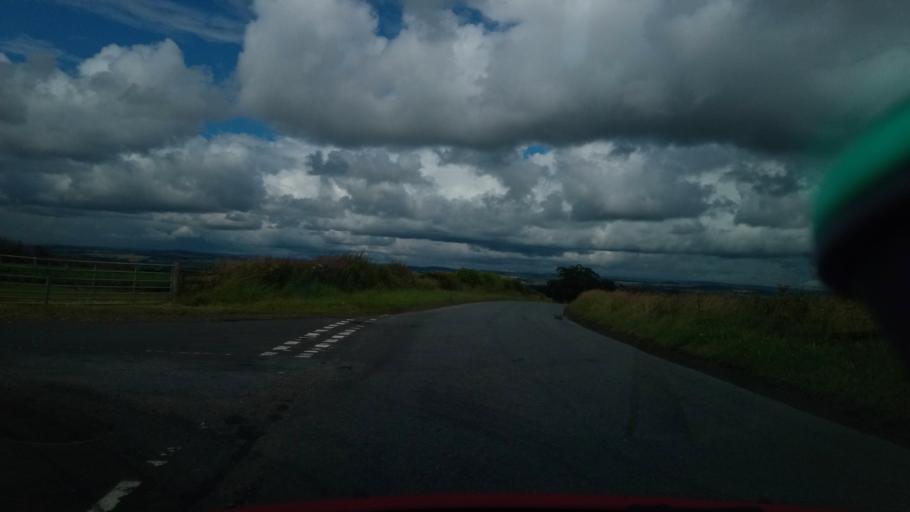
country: GB
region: Scotland
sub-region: The Scottish Borders
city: Kelso
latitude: 55.5657
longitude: -2.4150
